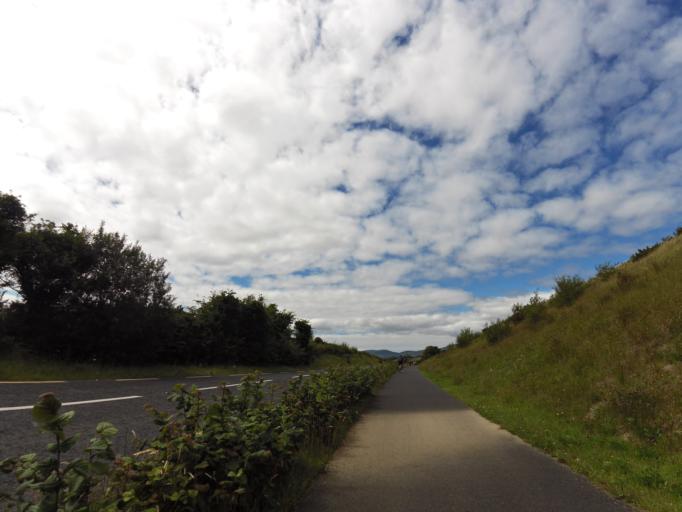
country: IE
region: Connaught
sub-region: Maigh Eo
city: Westport
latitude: 53.8758
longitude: -9.5432
